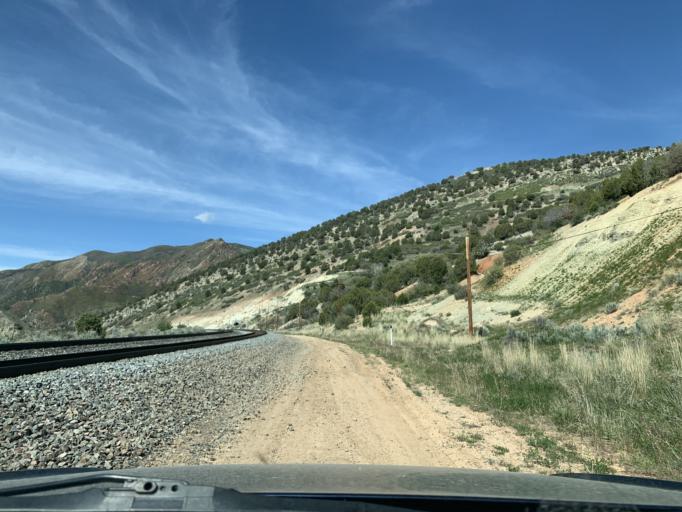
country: US
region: Utah
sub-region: Utah County
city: Mapleton
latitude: 39.9989
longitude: -111.4851
